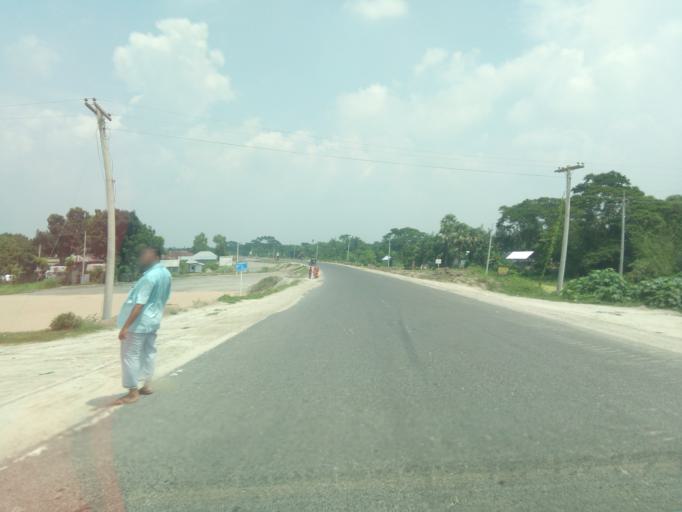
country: BD
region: Dhaka
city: Char Bhadrasan
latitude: 23.3797
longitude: 90.1203
